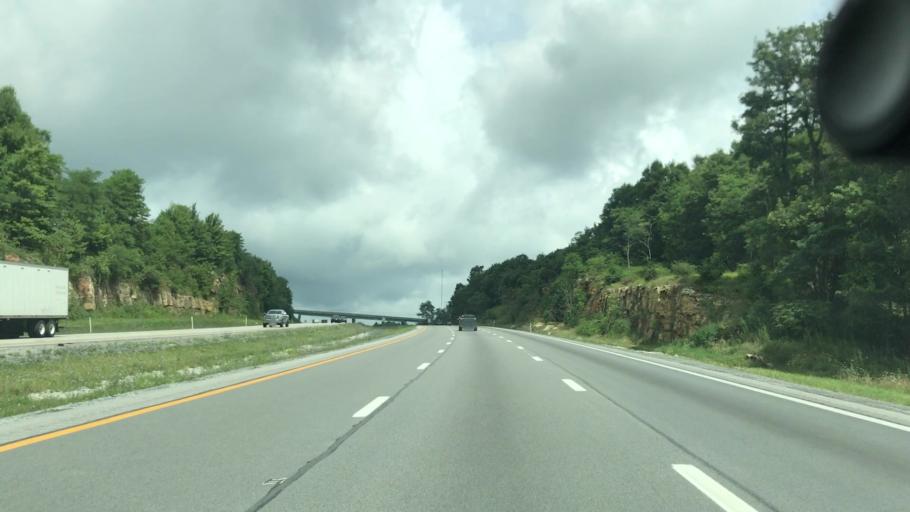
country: US
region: West Virginia
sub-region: Raleigh County
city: Shady Spring
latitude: 37.5777
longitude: -81.1158
